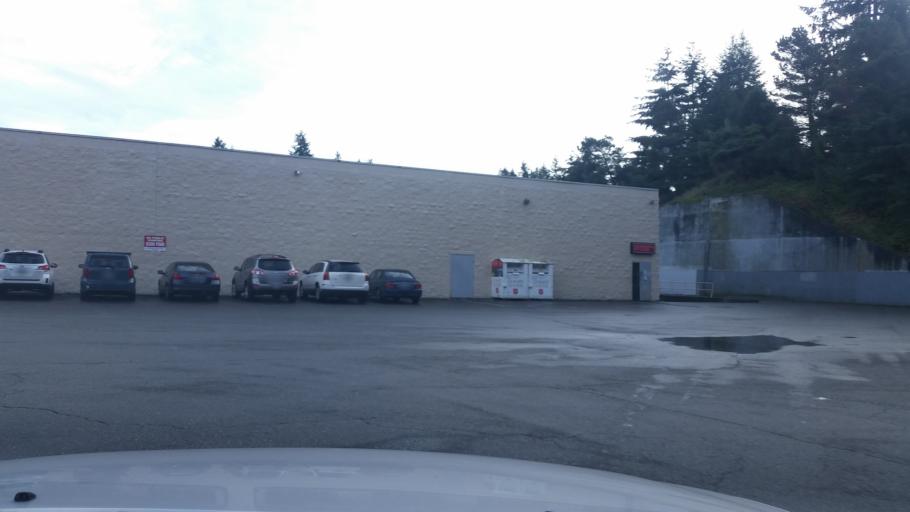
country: US
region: Washington
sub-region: King County
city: Shoreline
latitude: 47.7421
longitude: -122.3508
